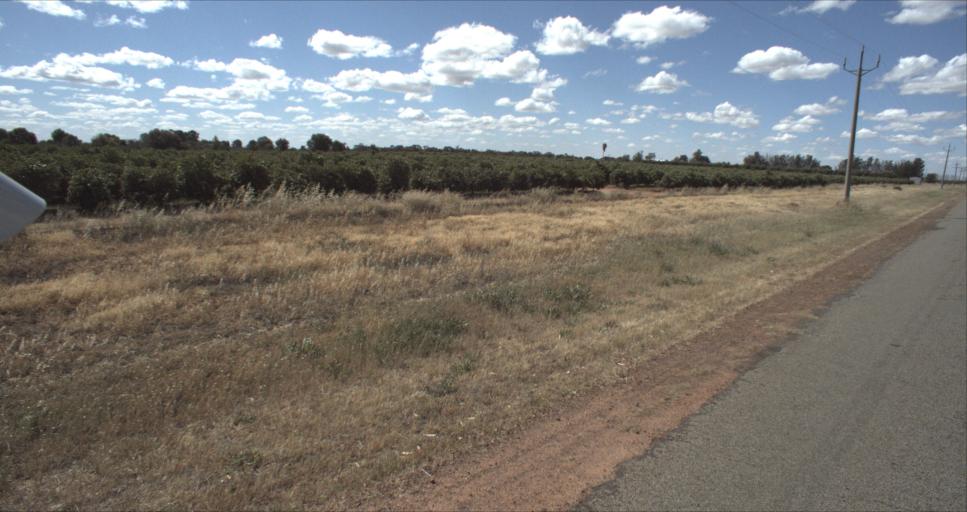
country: AU
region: New South Wales
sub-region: Leeton
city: Leeton
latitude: -34.5151
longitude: 146.2386
